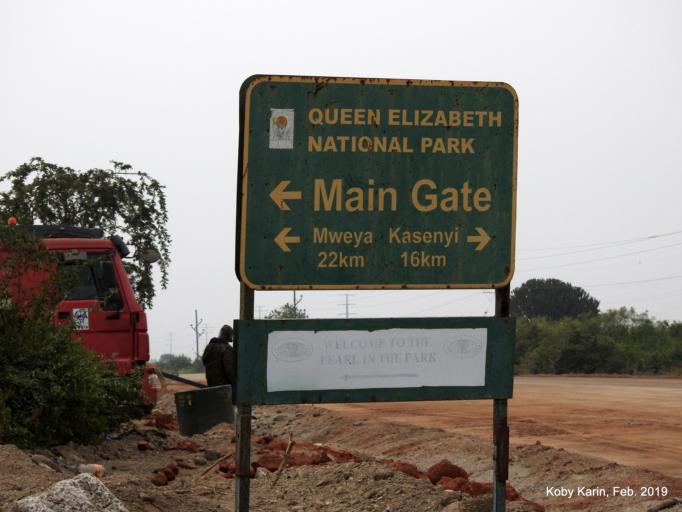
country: UG
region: Western Region
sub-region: Rubirizi District
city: Rubirizi
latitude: -0.0818
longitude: 30.0301
